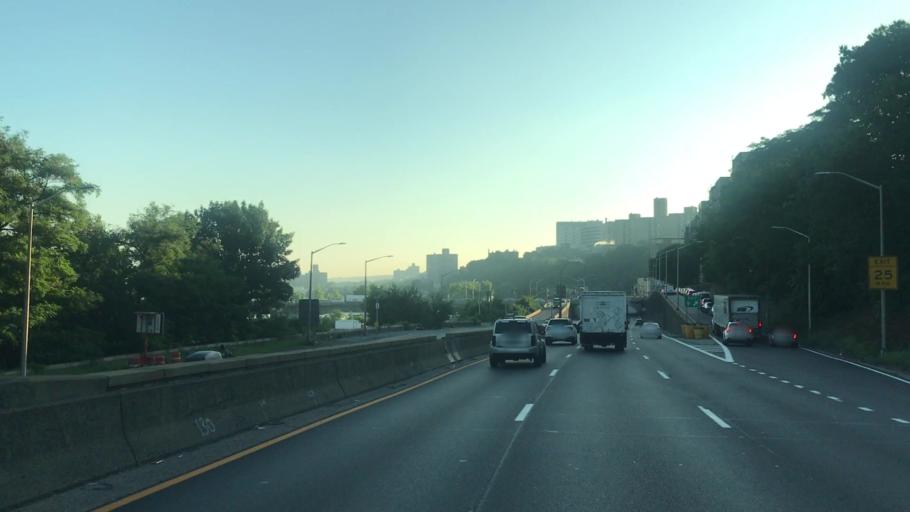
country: US
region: New York
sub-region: New York County
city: Inwood
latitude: 40.8594
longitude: -73.9158
